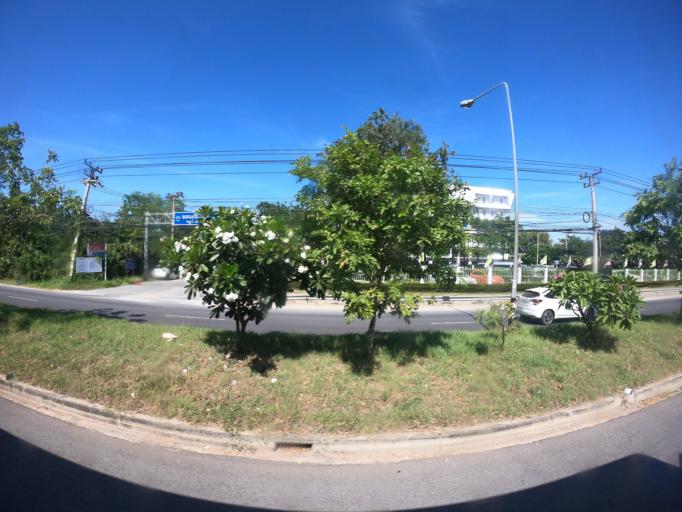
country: TH
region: Nakhon Ratchasima
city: Nakhon Ratchasima
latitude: 15.0136
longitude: 102.1280
